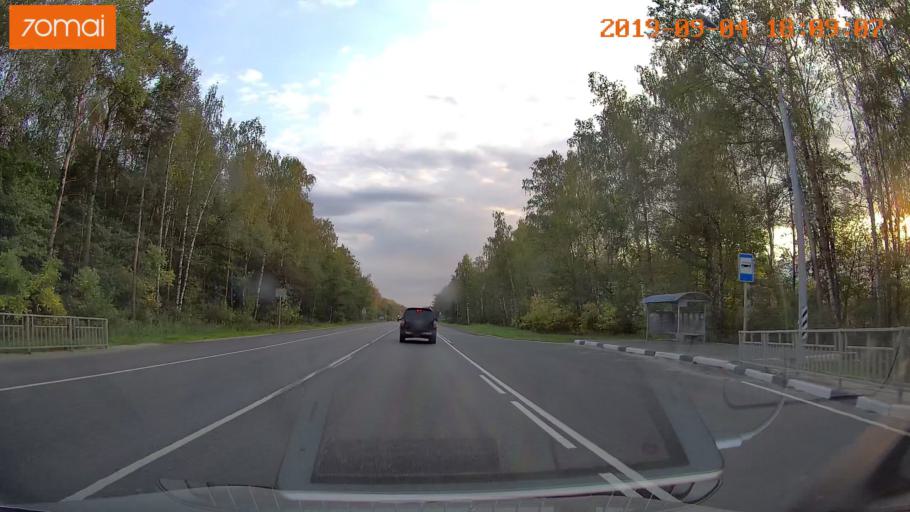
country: RU
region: Moskovskaya
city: Khorlovo
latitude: 55.3986
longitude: 38.7776
